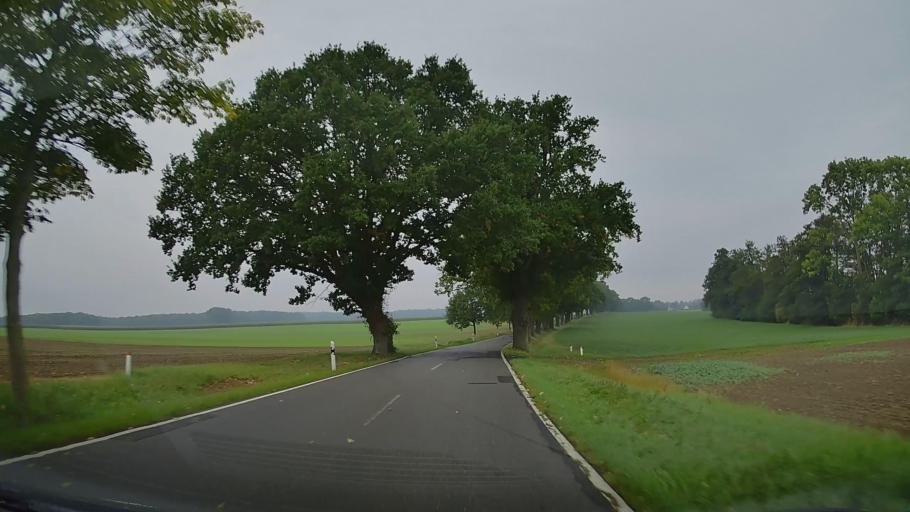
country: DE
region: Mecklenburg-Vorpommern
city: Kalkhorst
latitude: 53.9850
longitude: 11.0450
